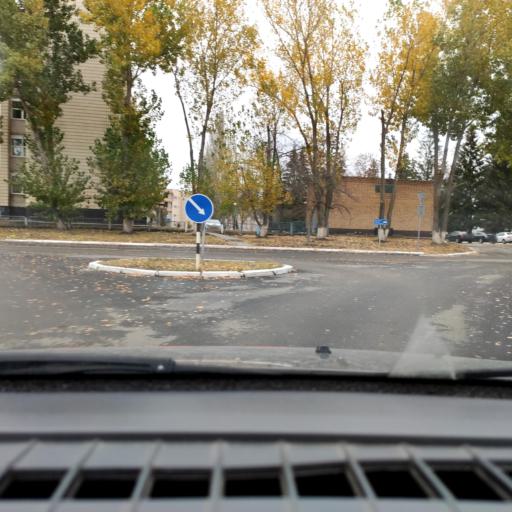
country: RU
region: Samara
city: Tol'yatti
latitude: 53.5228
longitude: 49.3290
